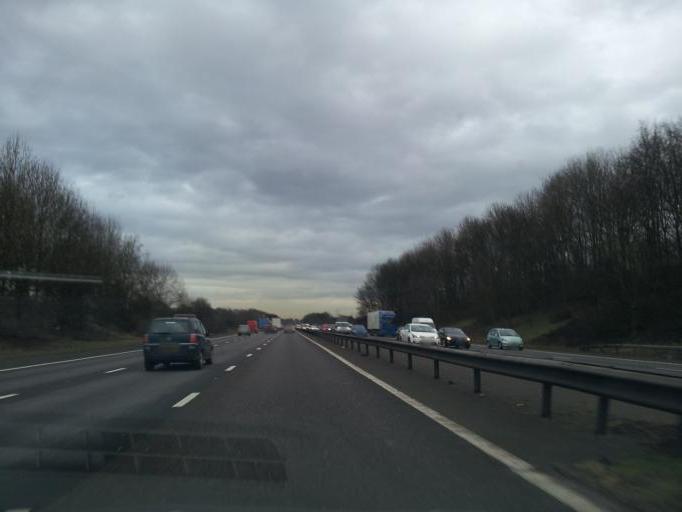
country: GB
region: England
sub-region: Coventry
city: Keresley
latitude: 52.4689
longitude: -1.5245
